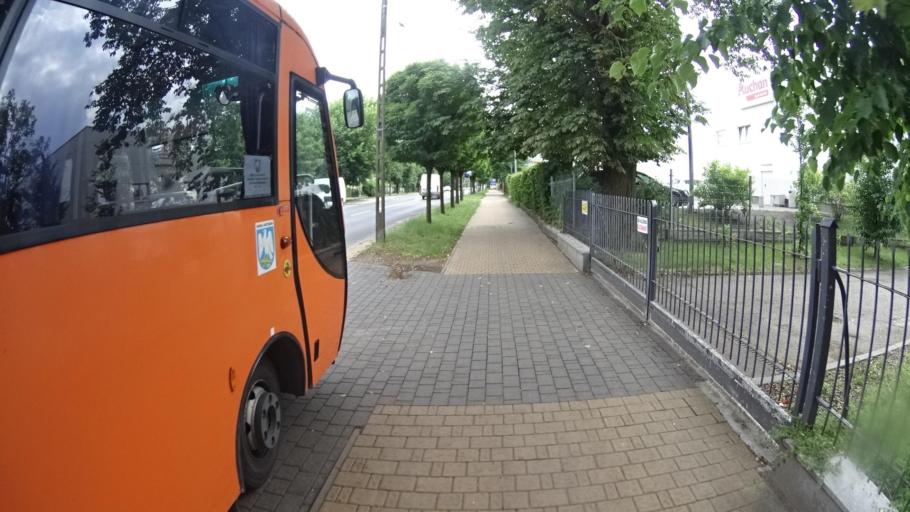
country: PL
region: Masovian Voivodeship
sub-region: Powiat grojecki
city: Grojec
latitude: 51.8615
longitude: 20.8678
